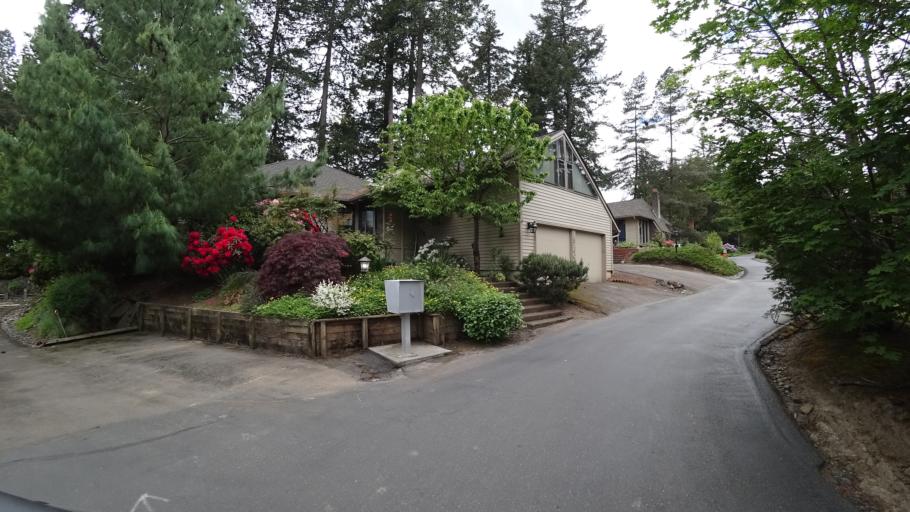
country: US
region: Oregon
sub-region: Washington County
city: Beaverton
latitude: 45.4754
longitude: -122.8331
